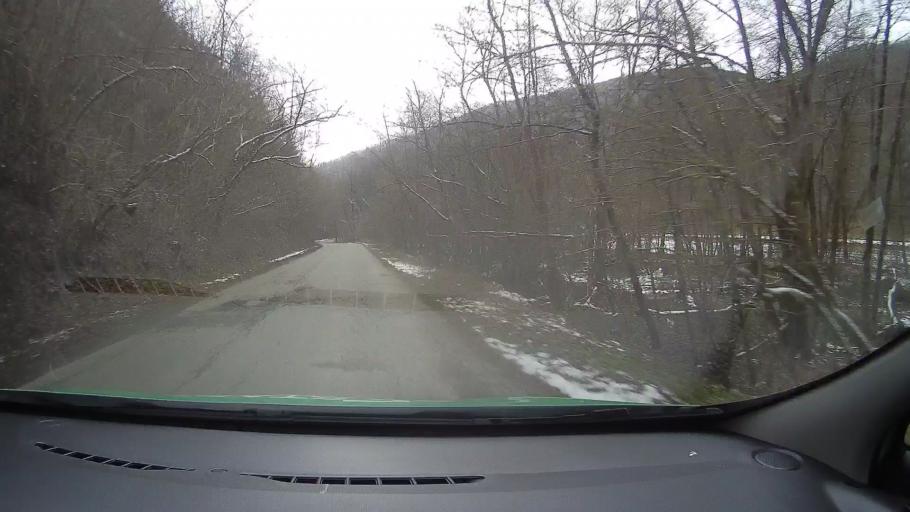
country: RO
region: Hunedoara
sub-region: Comuna Balsa
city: Balsa
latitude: 46.0080
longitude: 23.1513
